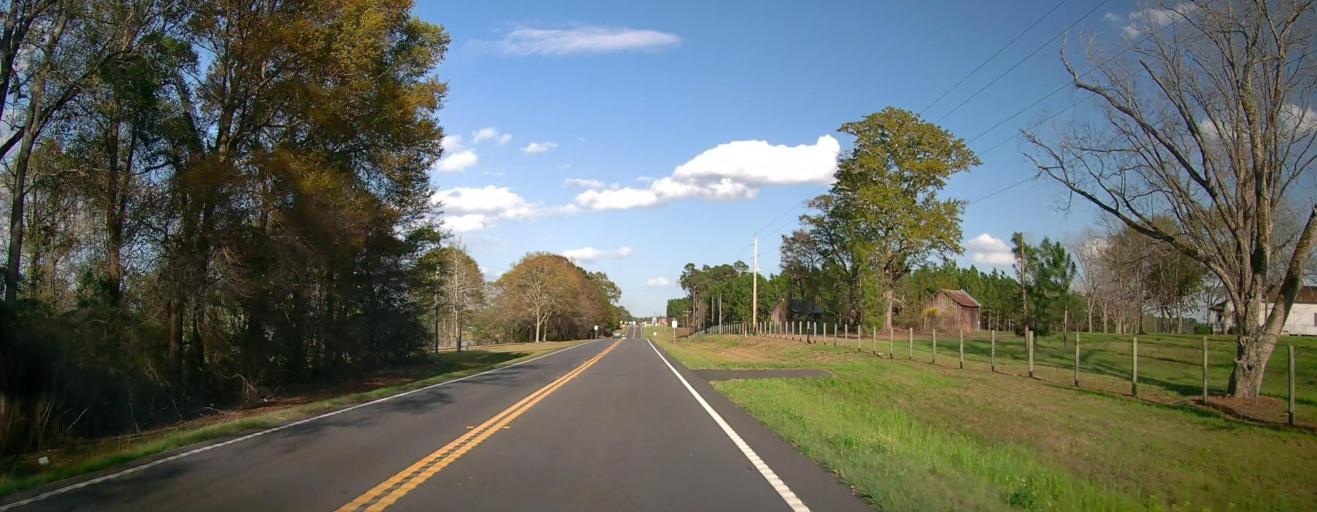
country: US
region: Georgia
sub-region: Toombs County
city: Vidalia
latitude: 32.2090
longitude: -82.4709
